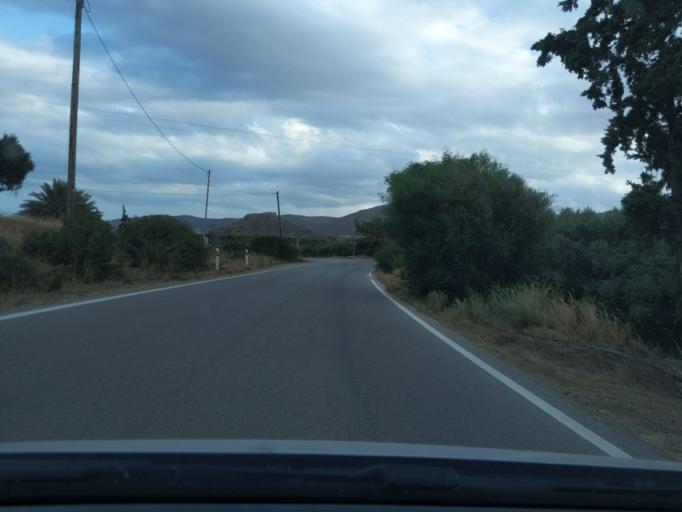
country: GR
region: Crete
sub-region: Nomos Lasithiou
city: Palekastro
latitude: 35.2167
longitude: 26.2642
